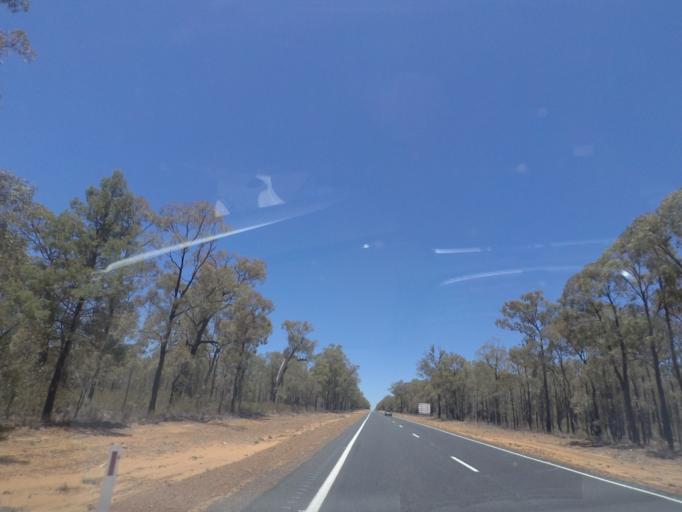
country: AU
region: New South Wales
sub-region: Narrabri
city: Narrabri
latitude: -30.7264
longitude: 149.5228
